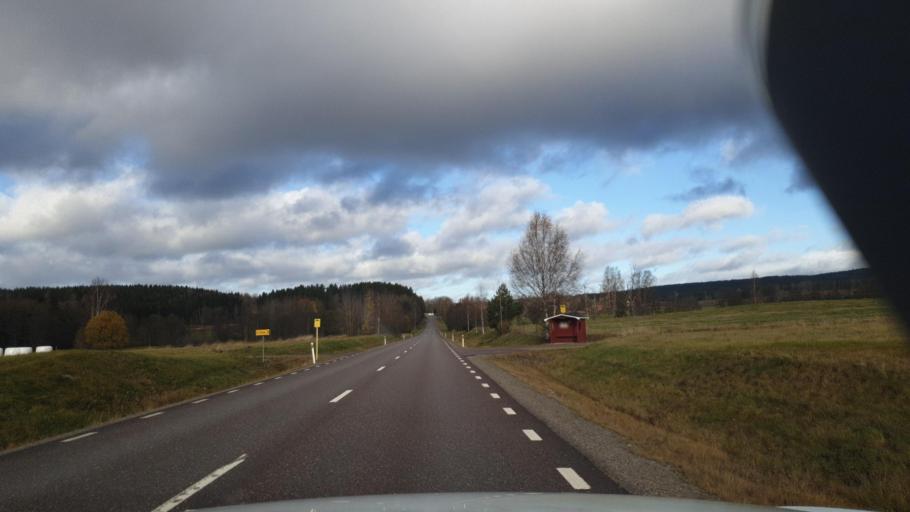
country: SE
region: Vaermland
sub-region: Arvika Kommun
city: Arvika
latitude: 59.4648
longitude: 12.7745
